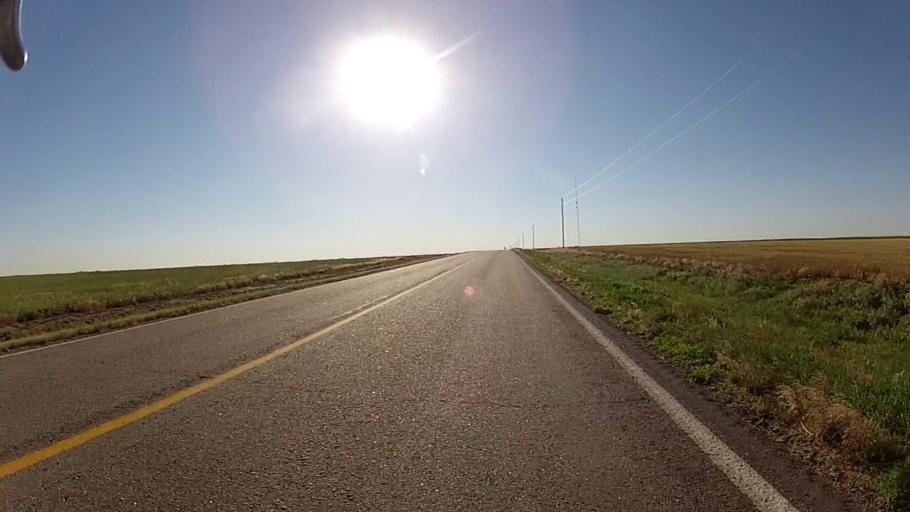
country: US
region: Kansas
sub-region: Ford County
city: Dodge City
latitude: 37.6464
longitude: -99.8503
